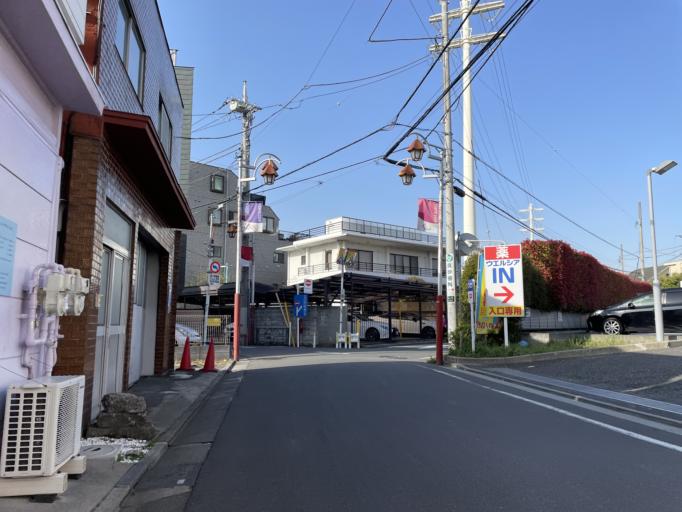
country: JP
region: Tokyo
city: Tokyo
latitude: 35.6920
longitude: 139.6414
